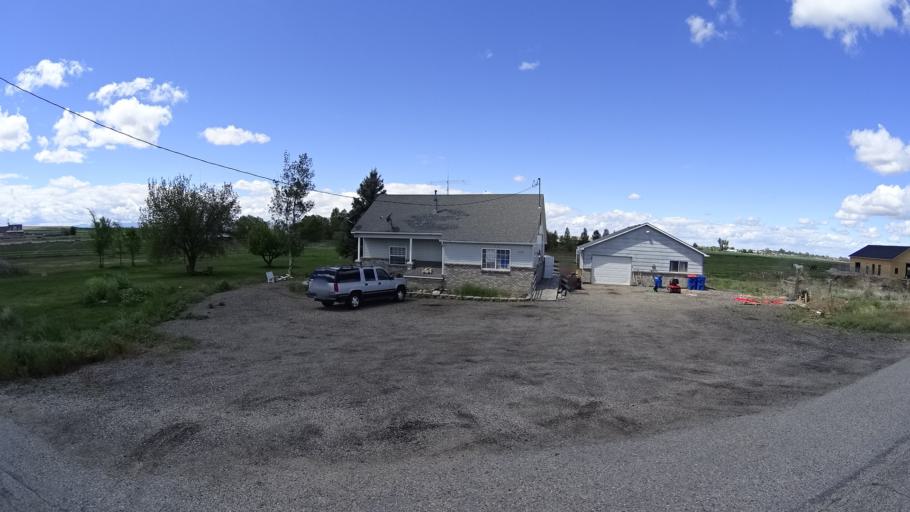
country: US
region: Idaho
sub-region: Ada County
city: Kuna
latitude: 43.4610
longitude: -116.3750
